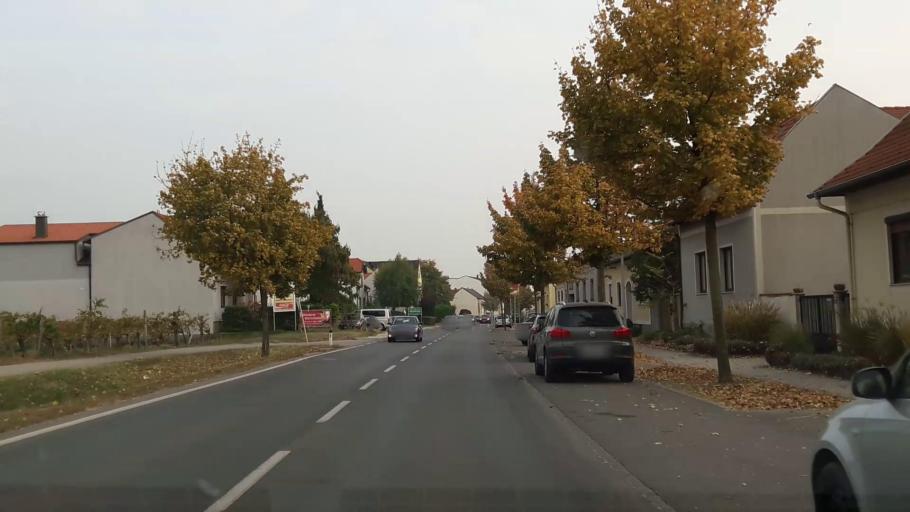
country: AT
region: Burgenland
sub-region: Politischer Bezirk Neusiedl am See
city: Weiden am See
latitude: 47.9330
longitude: 16.8612
